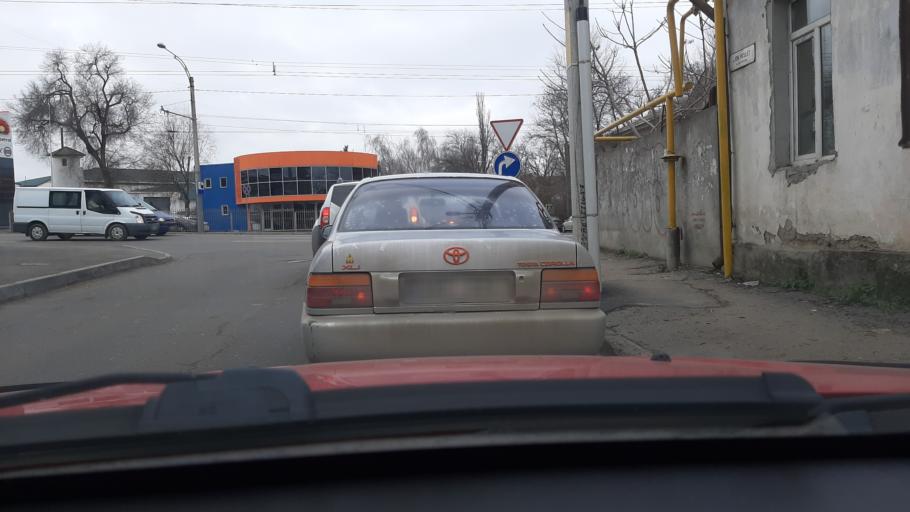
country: MD
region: Chisinau
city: Chisinau
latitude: 47.0097
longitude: 28.8375
